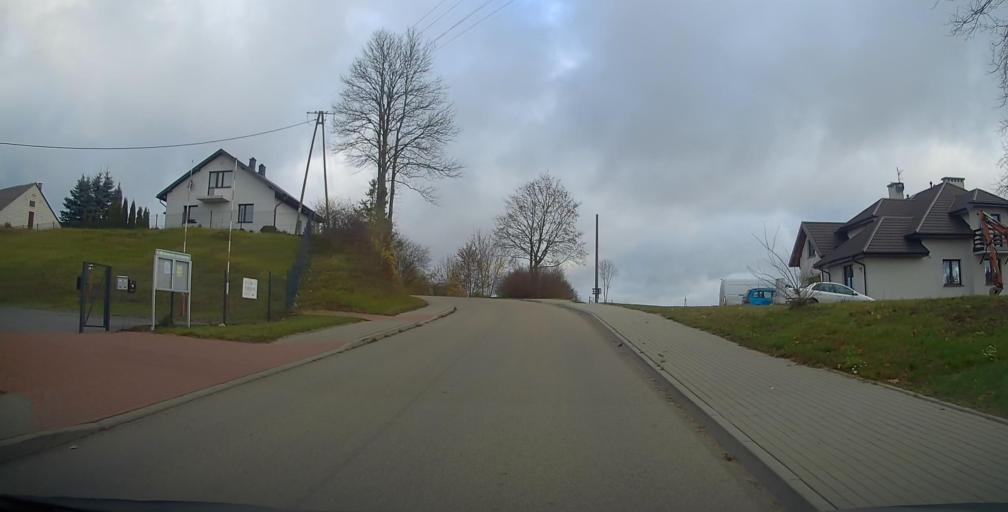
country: PL
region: Podlasie
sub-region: Suwalki
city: Suwalki
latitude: 54.2896
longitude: 22.8802
